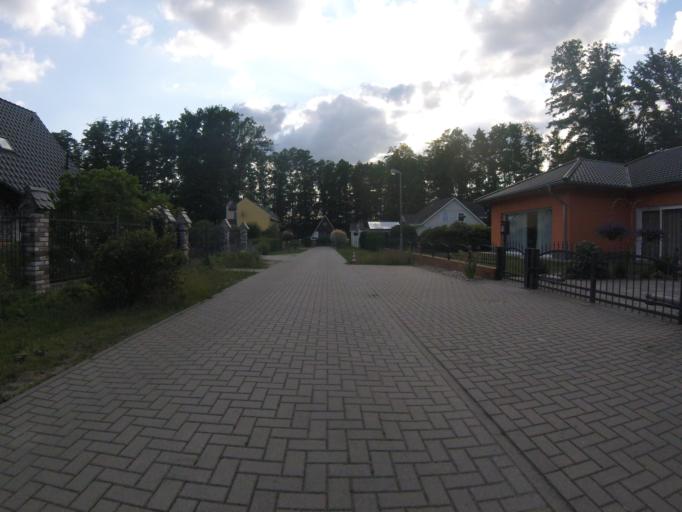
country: DE
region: Brandenburg
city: Bestensee
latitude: 52.2397
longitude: 13.6284
